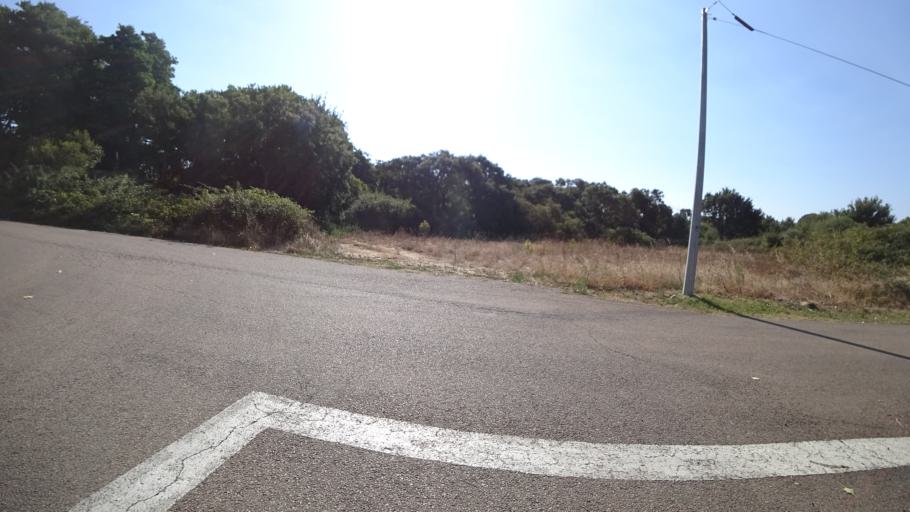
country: FR
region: Corsica
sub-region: Departement de la Corse-du-Sud
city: Porto-Vecchio
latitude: 41.6291
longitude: 9.3299
